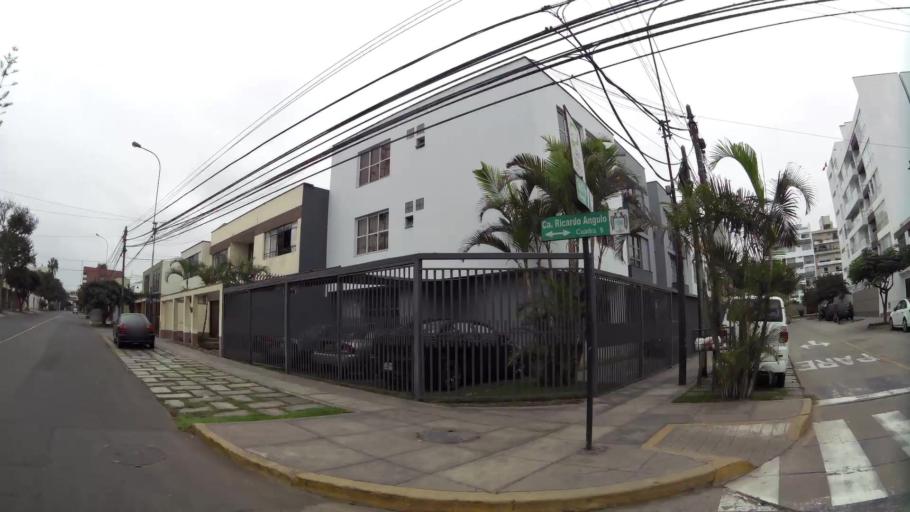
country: PE
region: Lima
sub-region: Lima
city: San Luis
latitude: -12.1015
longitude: -77.0150
